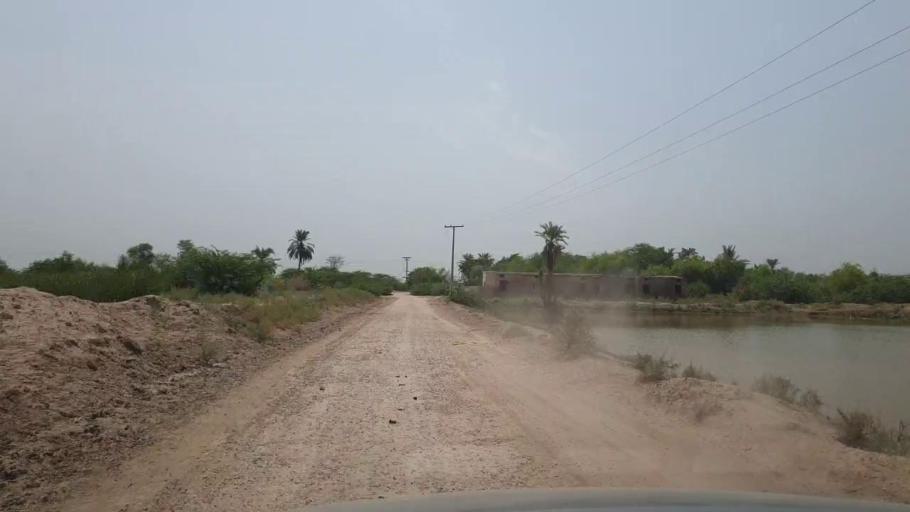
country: PK
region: Sindh
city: Garhi Yasin
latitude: 27.8786
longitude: 68.4953
